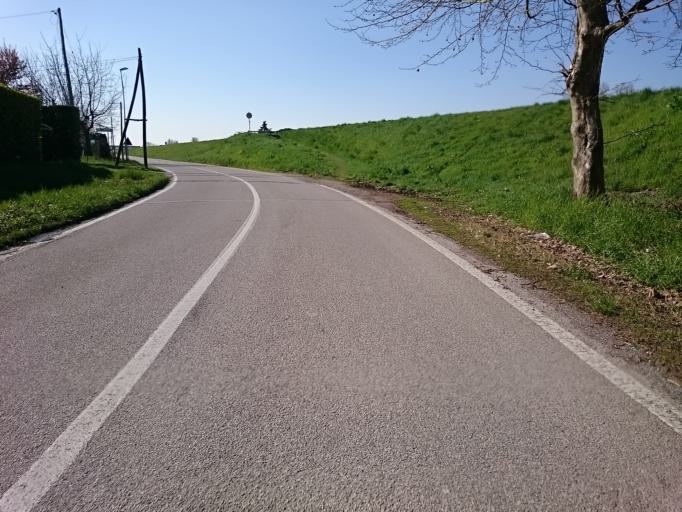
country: IT
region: Veneto
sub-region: Provincia di Padova
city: Ponte San Nicolo
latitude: 45.3825
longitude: 11.9172
